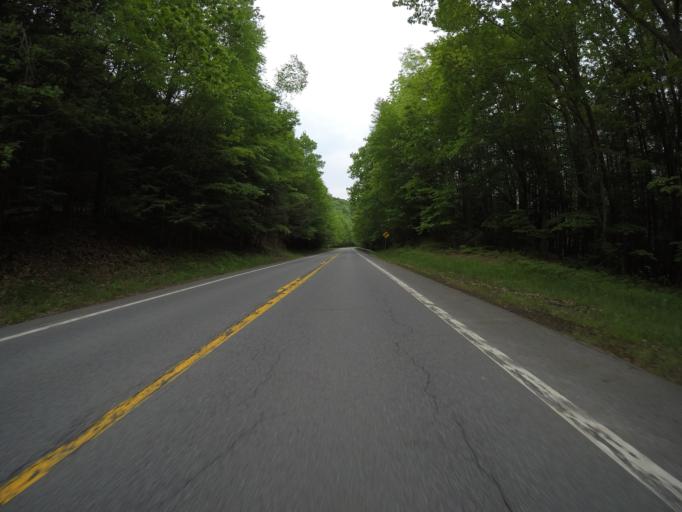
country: US
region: New York
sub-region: Sullivan County
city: Livingston Manor
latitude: 42.0766
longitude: -74.8755
